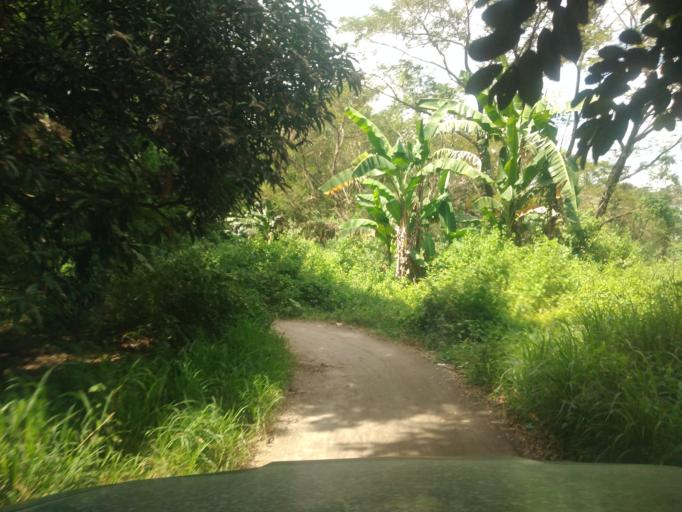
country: PH
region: Central Luzon
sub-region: Province of Pampanga
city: Balas
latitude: 15.0481
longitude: 120.5783
